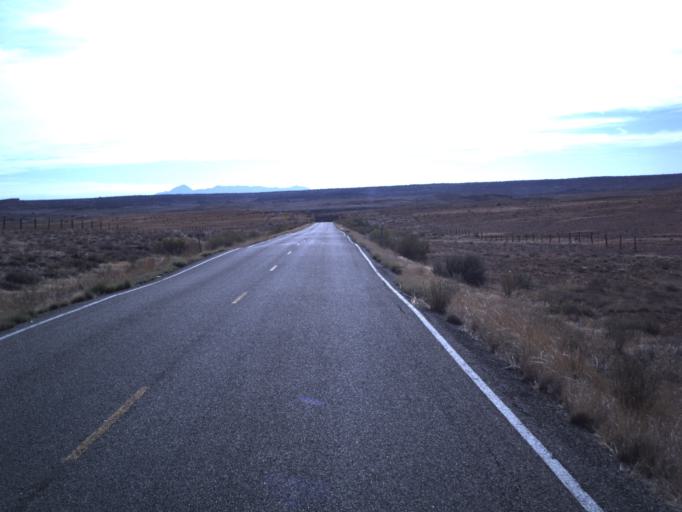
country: US
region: Utah
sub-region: San Juan County
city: Blanding
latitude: 37.4212
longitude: -109.4618
